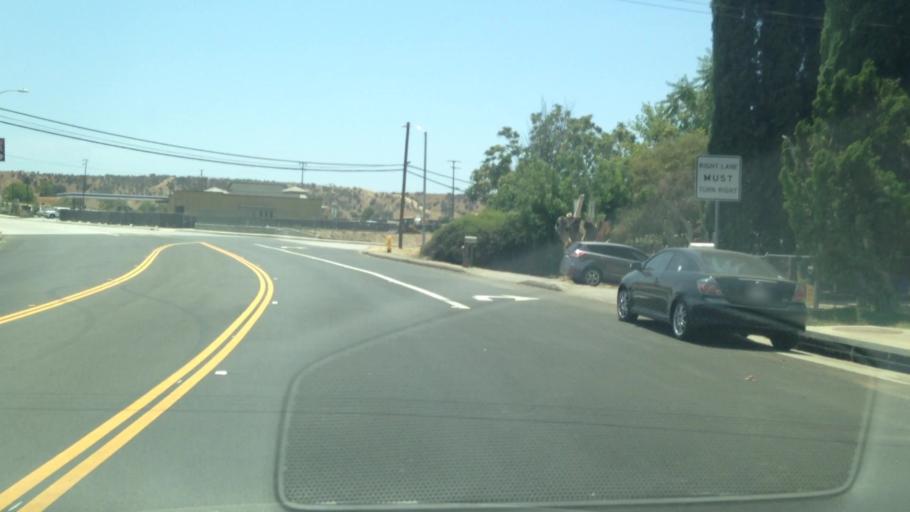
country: US
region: California
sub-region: Riverside County
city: Calimesa
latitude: 34.0202
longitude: -117.0955
